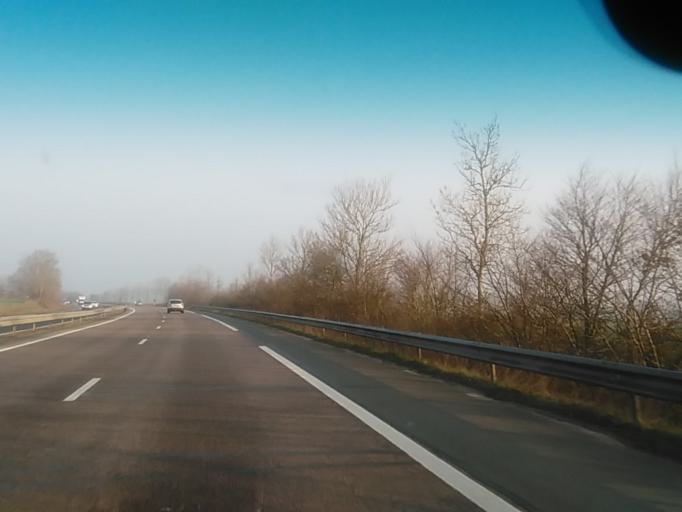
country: FR
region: Lower Normandy
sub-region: Departement du Calvados
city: Potigny
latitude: 48.9601
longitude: -0.2274
